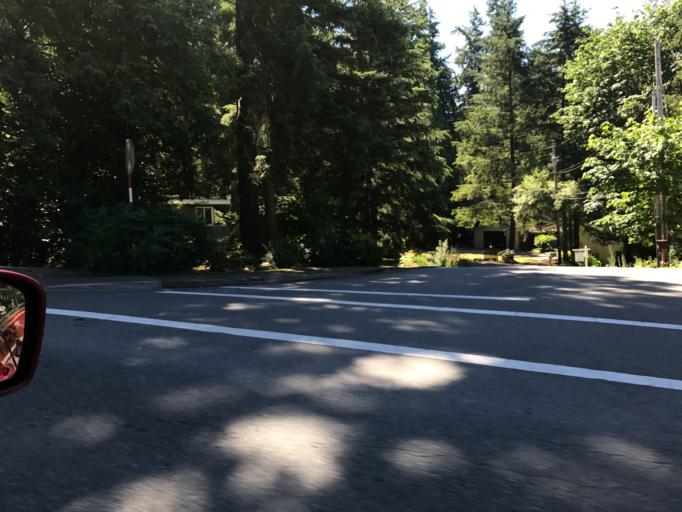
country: US
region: Washington
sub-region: King County
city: Bellevue
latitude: 47.6250
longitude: -122.1505
